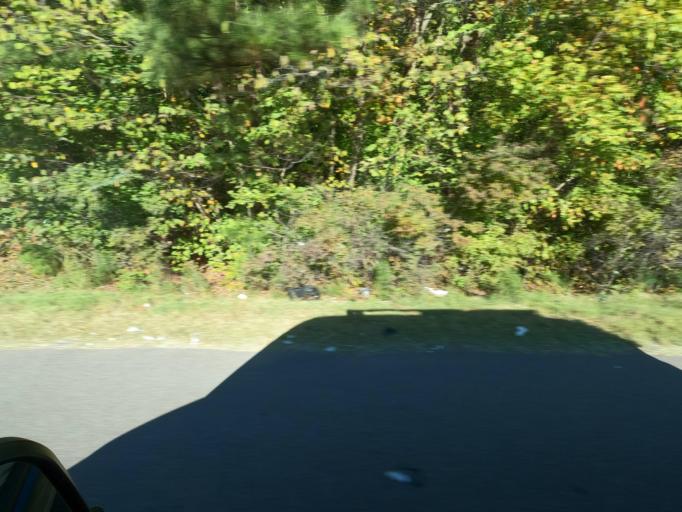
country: US
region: Tennessee
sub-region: Tipton County
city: Atoka
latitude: 35.4637
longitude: -89.7632
